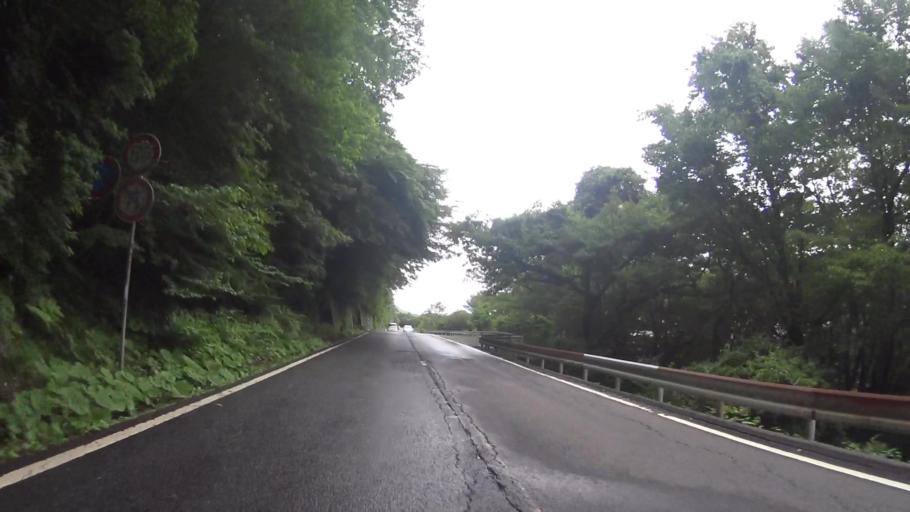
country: JP
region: Oita
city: Tsukawaki
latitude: 33.0978
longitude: 131.2206
